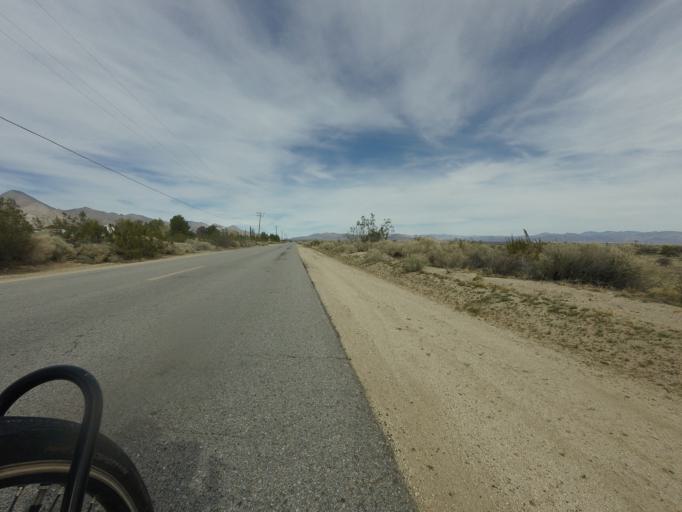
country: US
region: California
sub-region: Kern County
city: Inyokern
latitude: 35.7497
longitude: -117.8428
